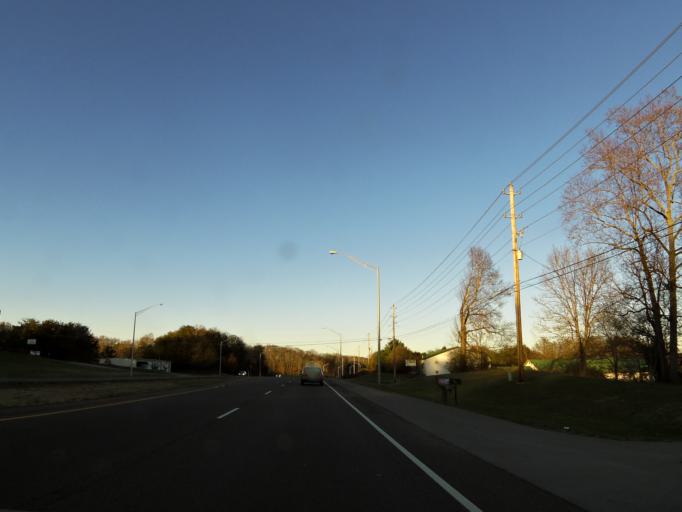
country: US
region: Tennessee
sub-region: Anderson County
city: Clinton
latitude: 36.1344
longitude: -84.1087
